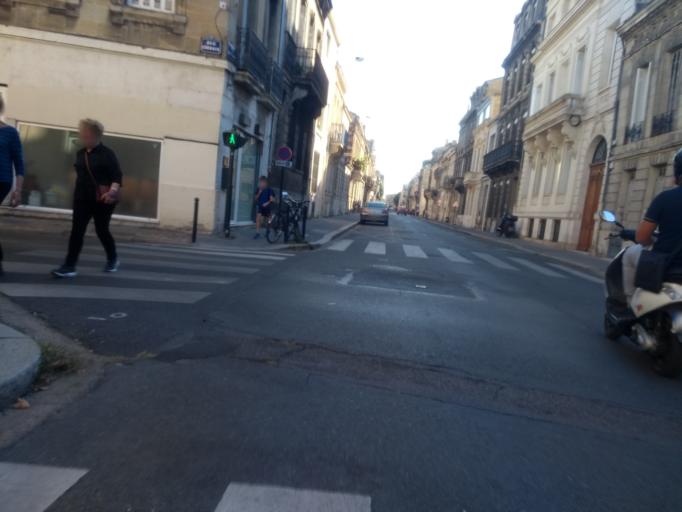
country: FR
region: Aquitaine
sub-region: Departement de la Gironde
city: Bordeaux
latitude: 44.8283
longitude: -0.5796
